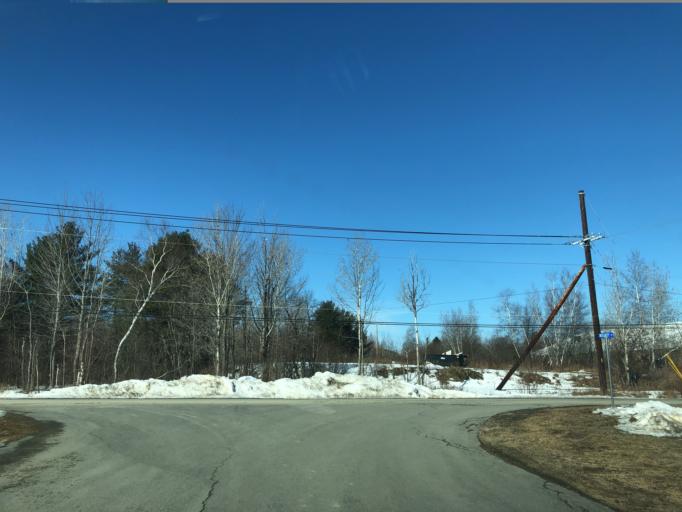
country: US
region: Maine
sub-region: Penobscot County
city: Brewer
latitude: 44.8242
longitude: -68.7444
